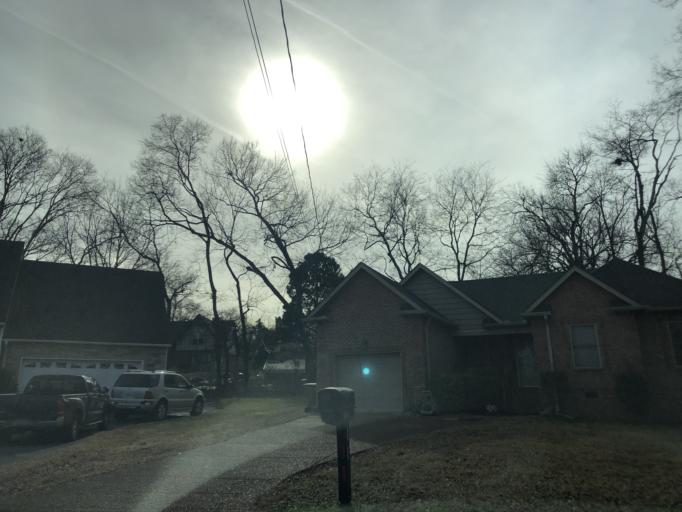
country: US
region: Tennessee
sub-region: Davidson County
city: Nashville
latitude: 36.2168
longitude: -86.7354
